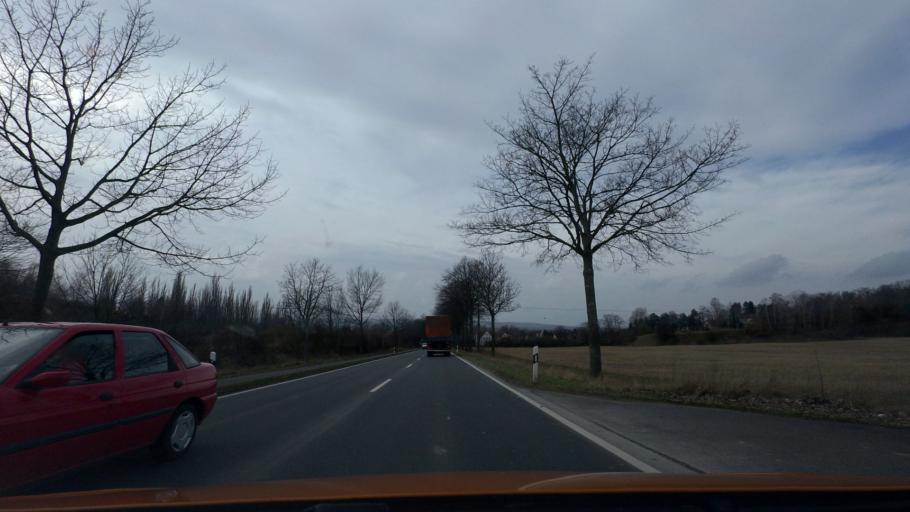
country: DE
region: Lower Saxony
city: Supplingen
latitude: 52.2265
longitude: 10.9177
